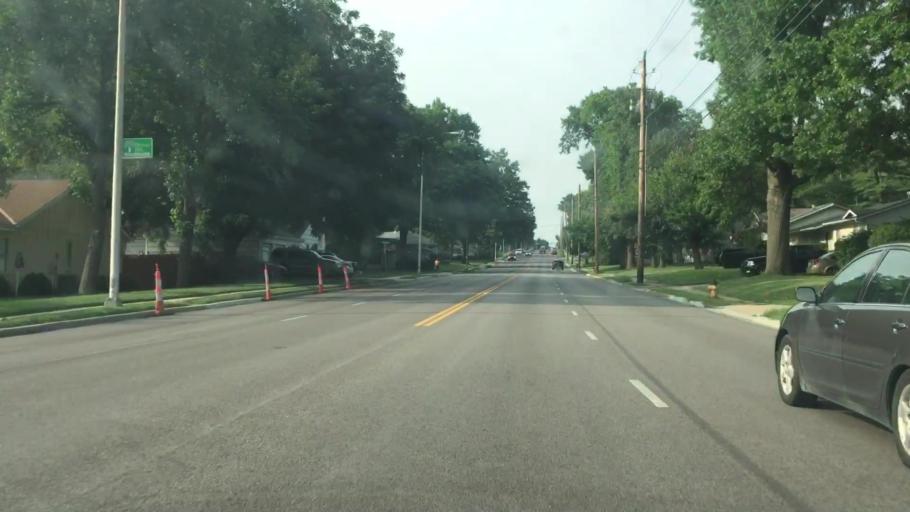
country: US
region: Kansas
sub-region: Johnson County
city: Overland Park
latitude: 38.9582
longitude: -94.6864
